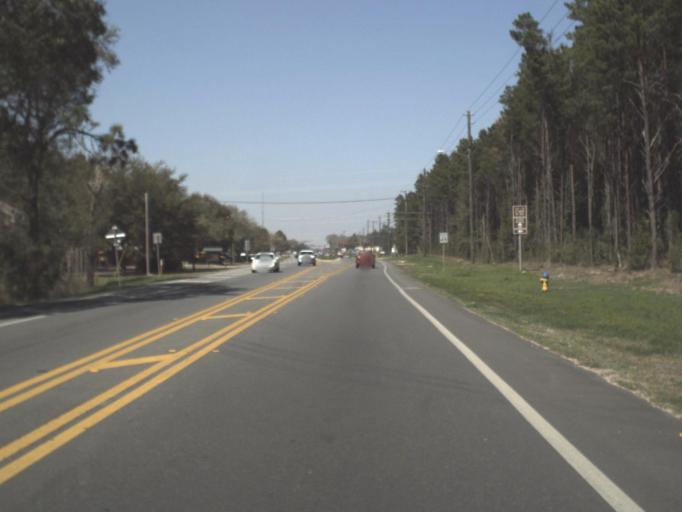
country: US
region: Florida
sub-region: Leon County
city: Woodville
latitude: 30.3699
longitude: -84.2676
